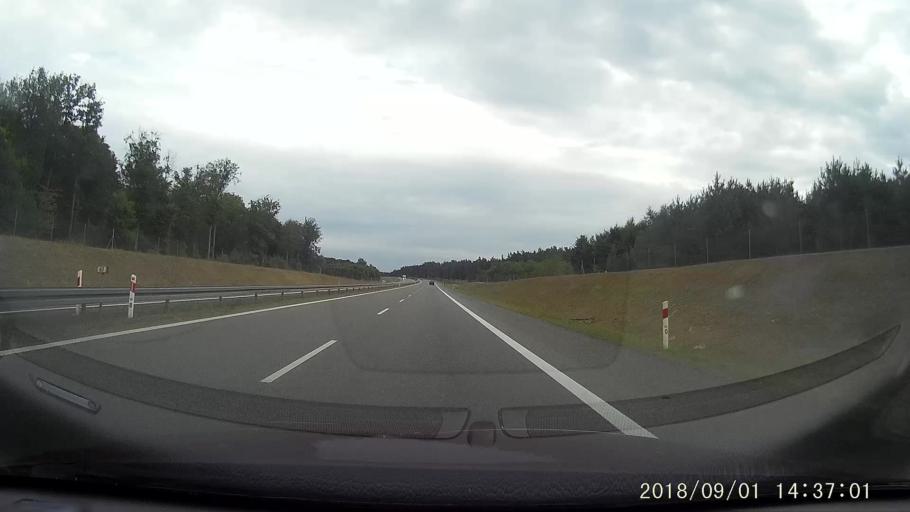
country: PL
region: West Pomeranian Voivodeship
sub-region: Powiat mysliborski
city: Nowogrodek Pomorski
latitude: 52.8535
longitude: 15.0390
